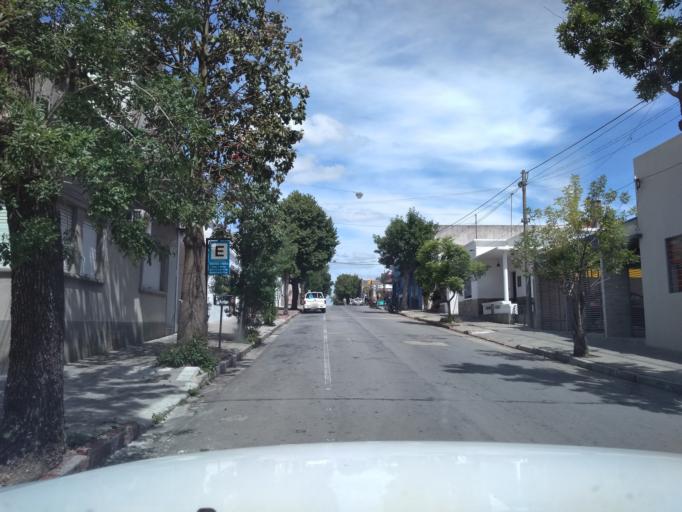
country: UY
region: Florida
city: Florida
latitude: -34.1000
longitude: -56.2169
